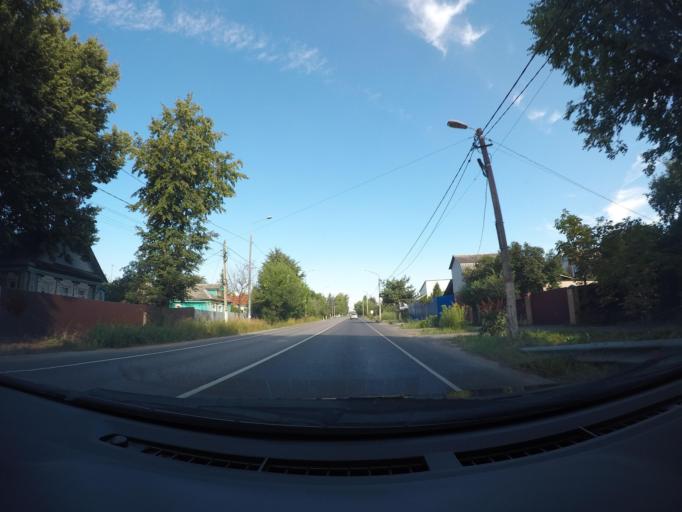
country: RU
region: Moskovskaya
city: Gzhel'
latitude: 55.6212
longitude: 38.3781
